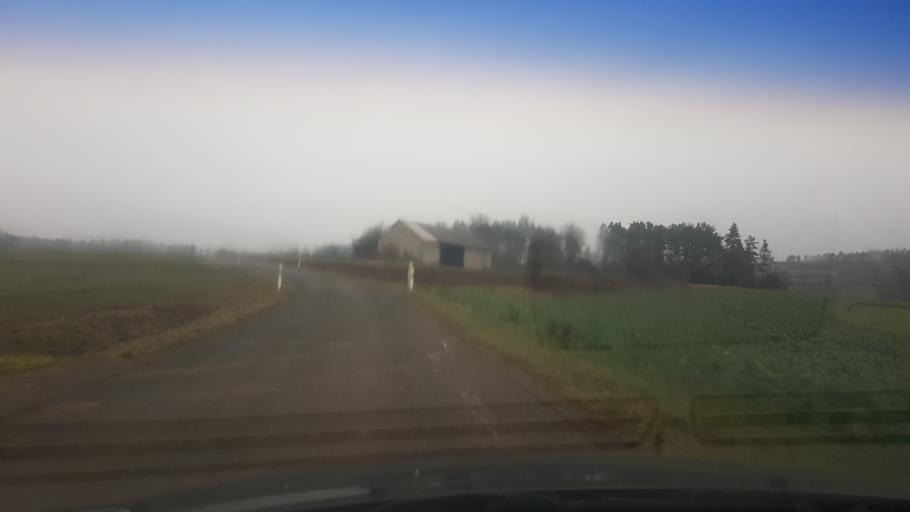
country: DE
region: Bavaria
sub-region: Upper Franconia
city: Weismain
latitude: 50.0550
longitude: 11.2880
